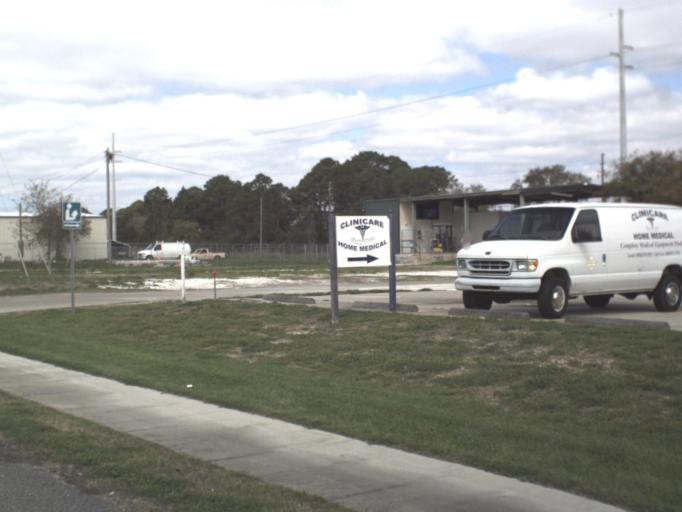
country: US
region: Florida
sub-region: Franklin County
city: Eastpoint
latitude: 29.7359
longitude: -84.8941
